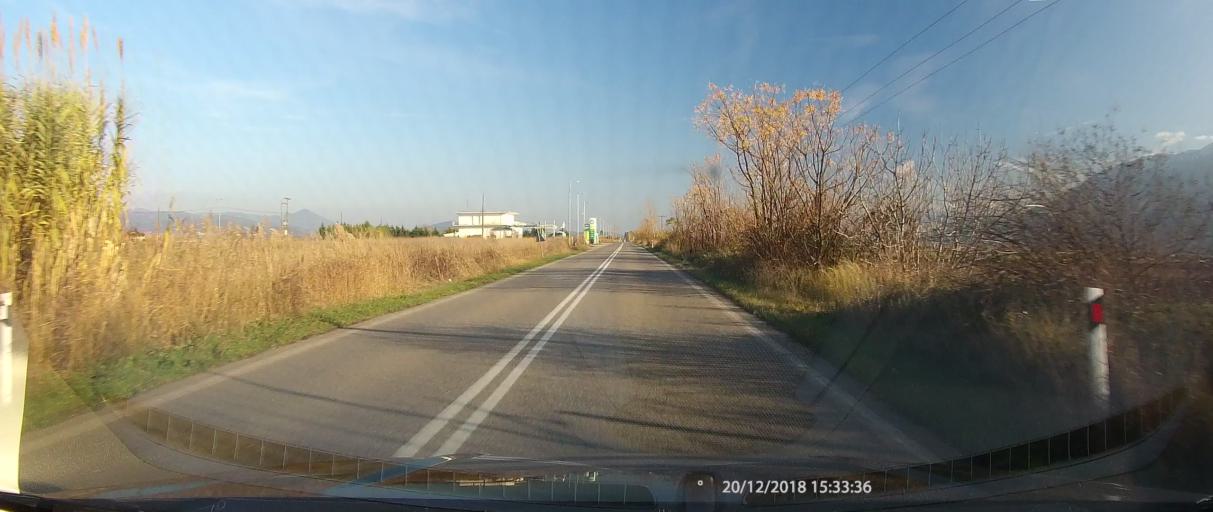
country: GR
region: Central Greece
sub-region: Nomos Fthiotidos
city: Lianokladhion
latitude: 38.9229
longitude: 22.2793
